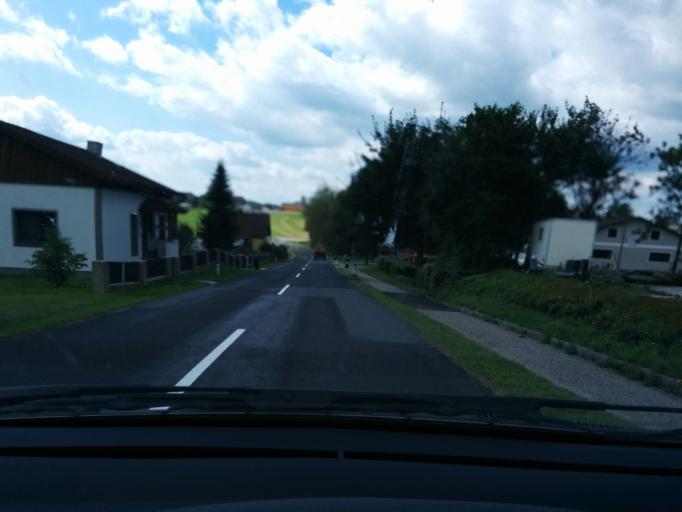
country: AT
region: Upper Austria
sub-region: Politischer Bezirk Rohrbach
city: Ulrichsberg
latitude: 48.6995
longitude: 13.8855
